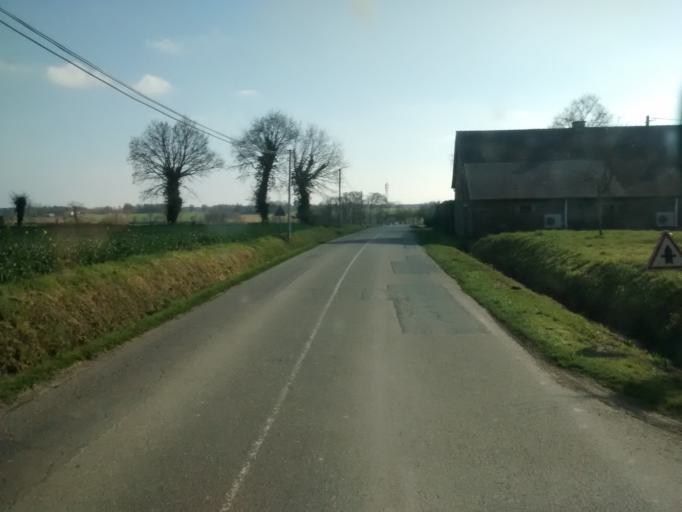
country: FR
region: Brittany
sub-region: Departement d'Ille-et-Vilaine
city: Maxent
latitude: 47.9765
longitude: -2.0225
